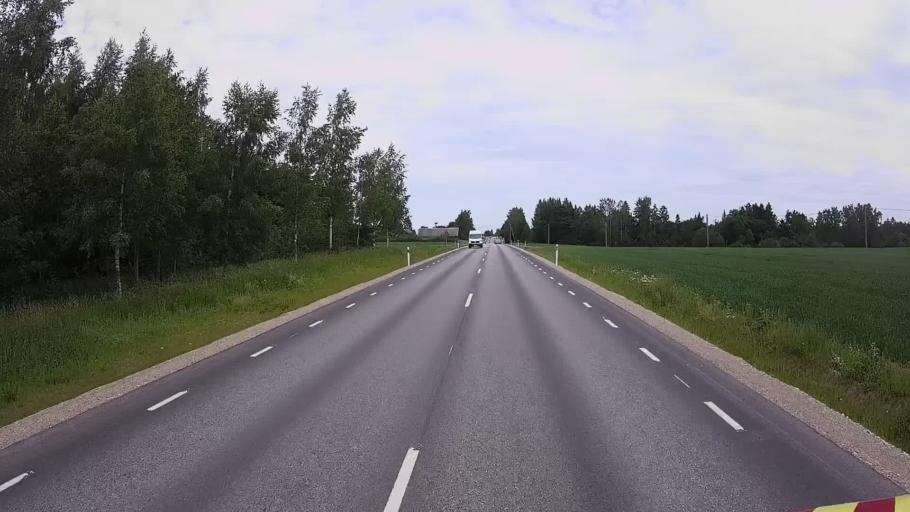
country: EE
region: Viljandimaa
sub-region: Viljandi linn
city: Viljandi
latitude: 58.2599
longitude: 25.5877
